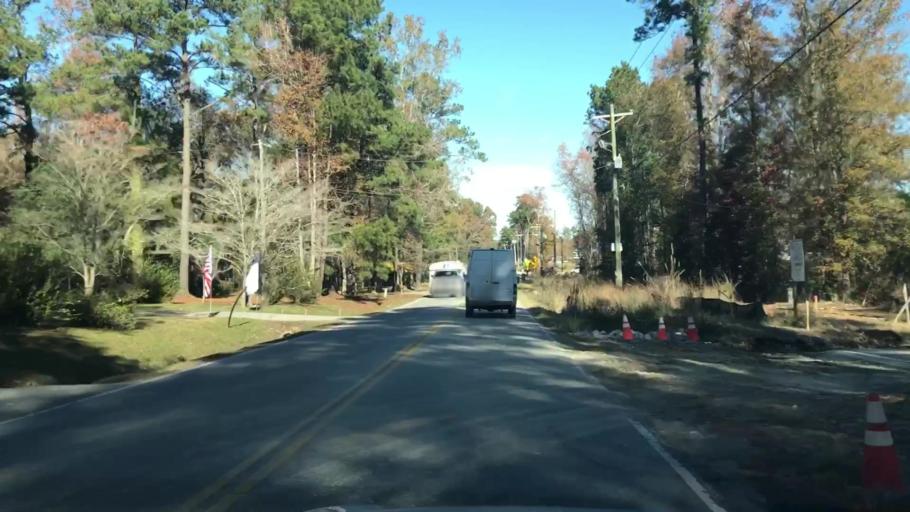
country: US
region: South Carolina
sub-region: Dorchester County
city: Summerville
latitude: 33.0207
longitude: -80.2411
